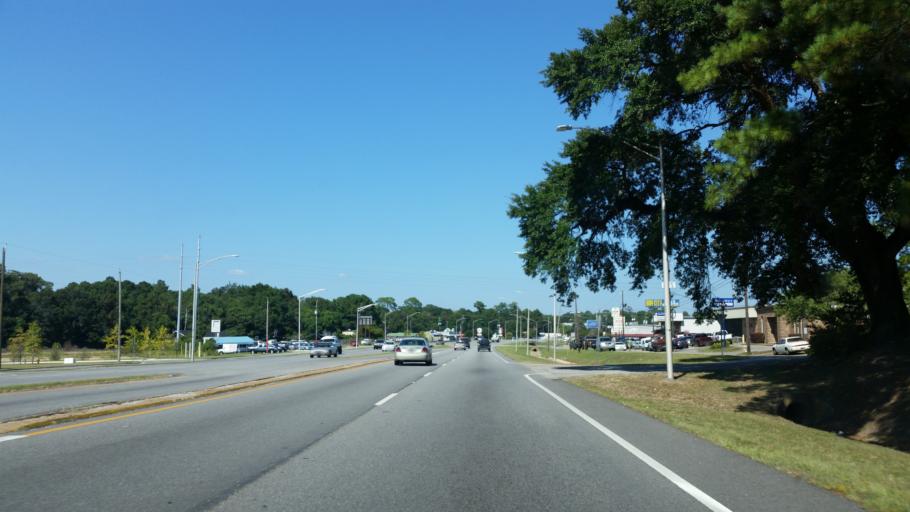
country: US
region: Alabama
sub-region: Mobile County
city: Mobile
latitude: 30.6688
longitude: -88.1033
